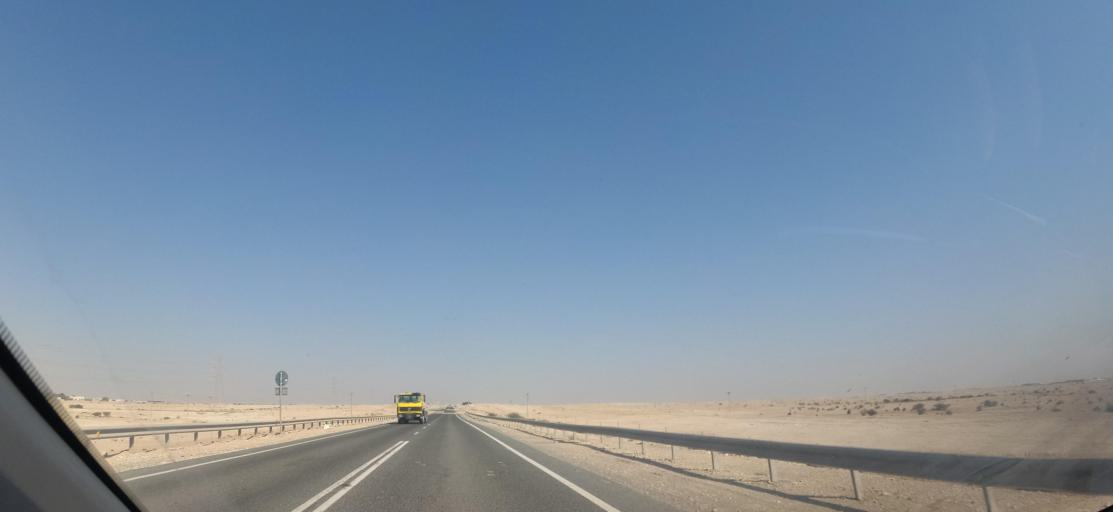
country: QA
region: Baladiyat ar Rayyan
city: Dukhan
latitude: 25.4739
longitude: 50.9395
